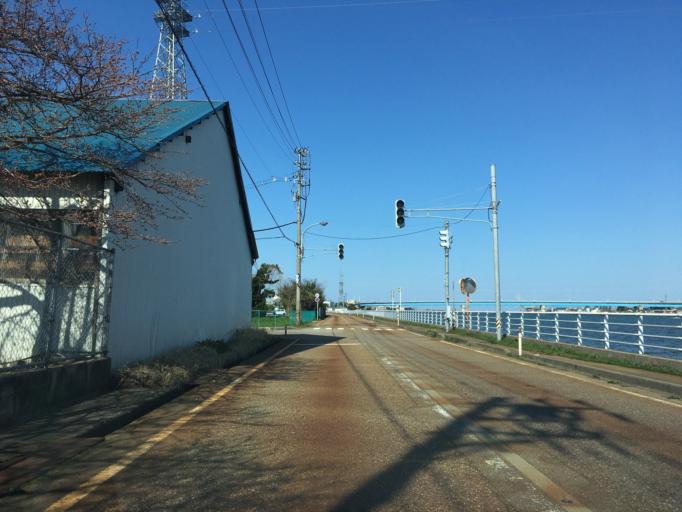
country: JP
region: Toyama
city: Nishishinminato
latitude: 36.7850
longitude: 137.0525
